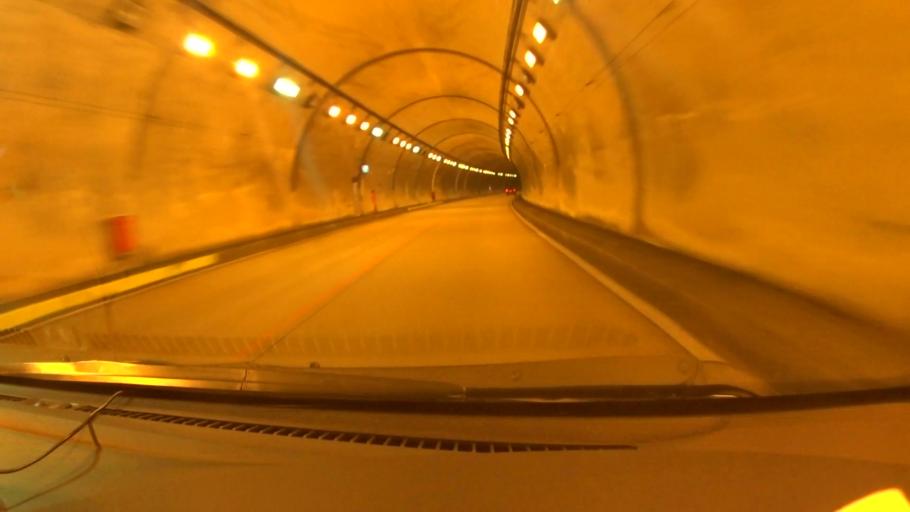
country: JP
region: Kyoto
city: Kameoka
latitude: 34.9937
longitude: 135.5766
